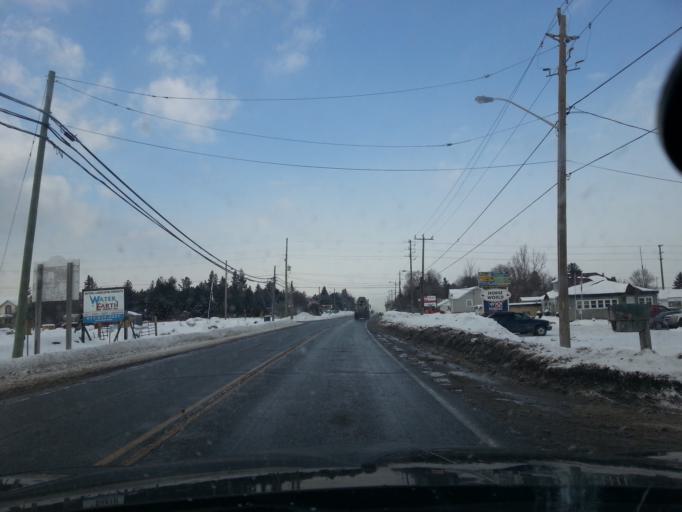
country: CA
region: Ontario
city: Bells Corners
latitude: 45.2719
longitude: -75.9453
